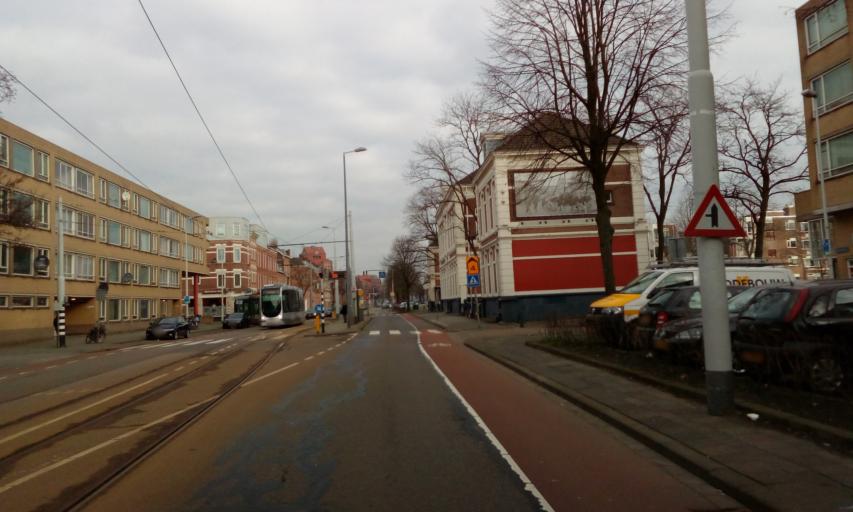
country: NL
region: South Holland
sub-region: Gemeente Rotterdam
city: Rotterdam
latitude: 51.9316
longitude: 4.4973
